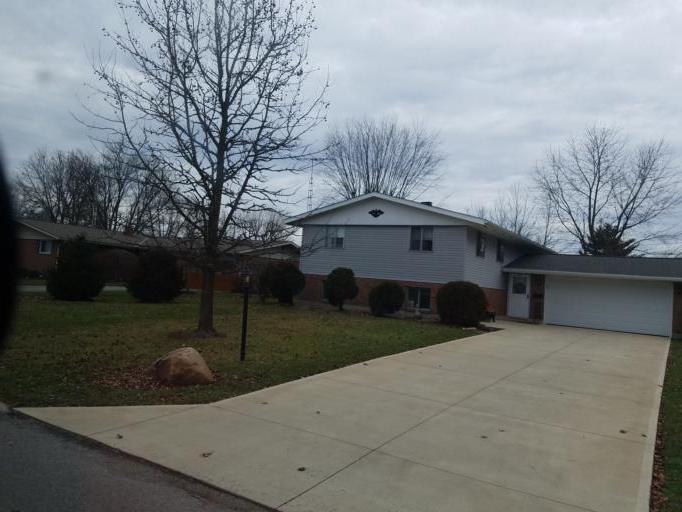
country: US
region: Ohio
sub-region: Marion County
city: Marion
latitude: 40.5745
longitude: -83.0828
